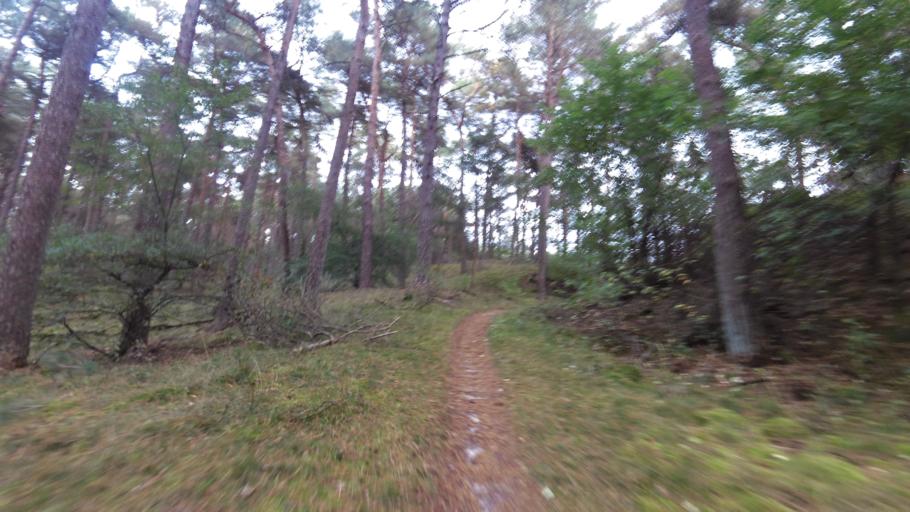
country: NL
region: Gelderland
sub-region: Gemeente Ede
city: Harskamp
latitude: 52.1625
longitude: 5.7402
